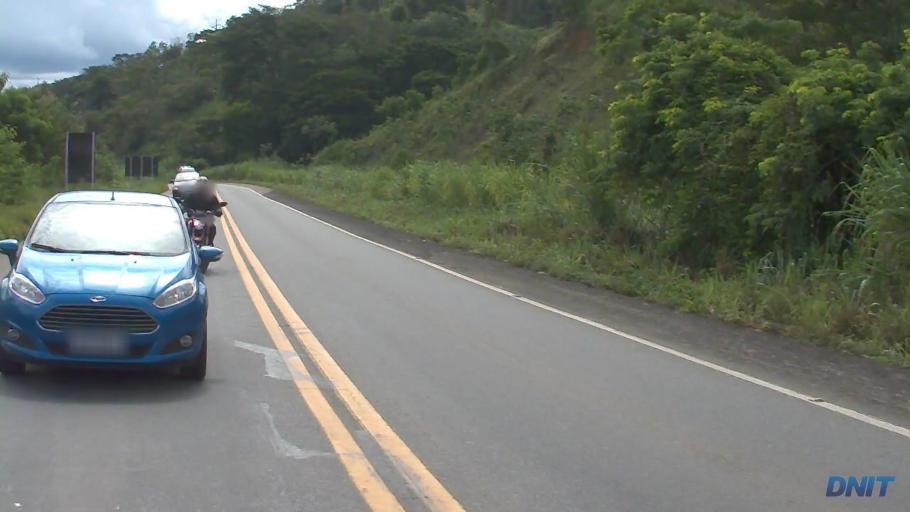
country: BR
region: Minas Gerais
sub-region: Ipaba
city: Ipaba
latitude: -19.3627
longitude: -42.4483
